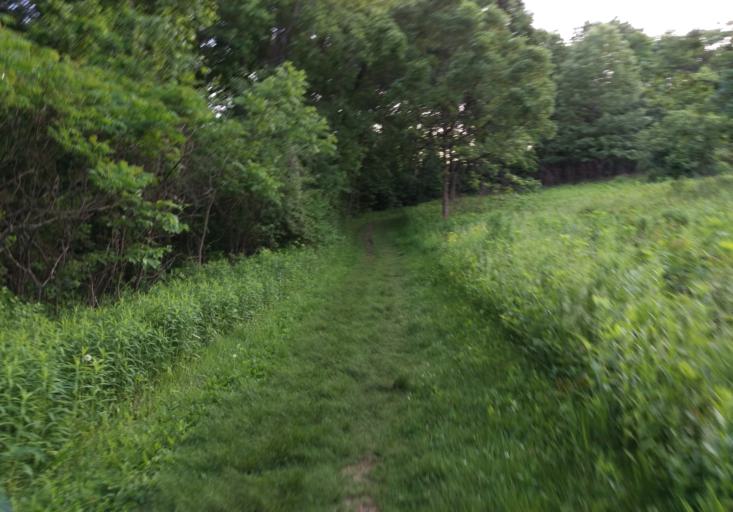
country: US
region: Wisconsin
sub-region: Dane County
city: Middleton
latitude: 43.0696
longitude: -89.4840
